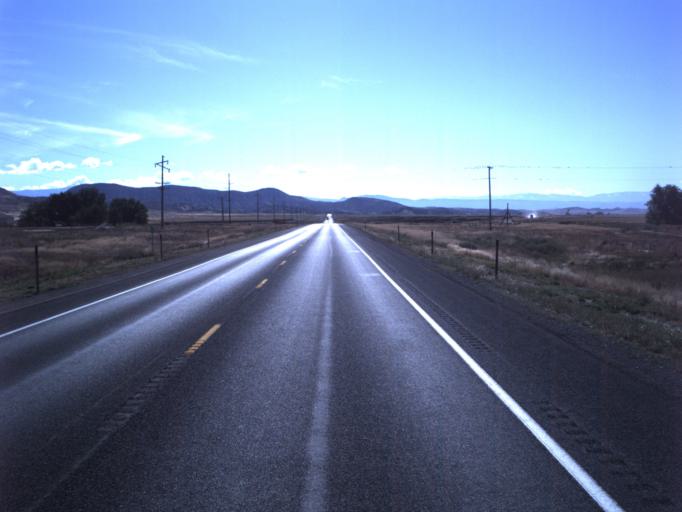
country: US
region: Utah
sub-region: Sanpete County
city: Gunnison
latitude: 39.2637
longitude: -111.8672
